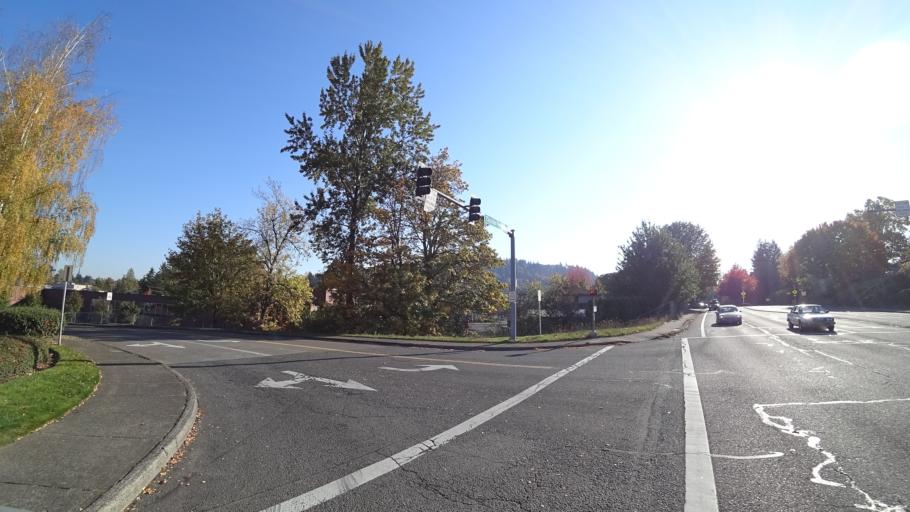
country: US
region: Oregon
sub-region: Multnomah County
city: Gresham
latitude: 45.4995
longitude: -122.4366
